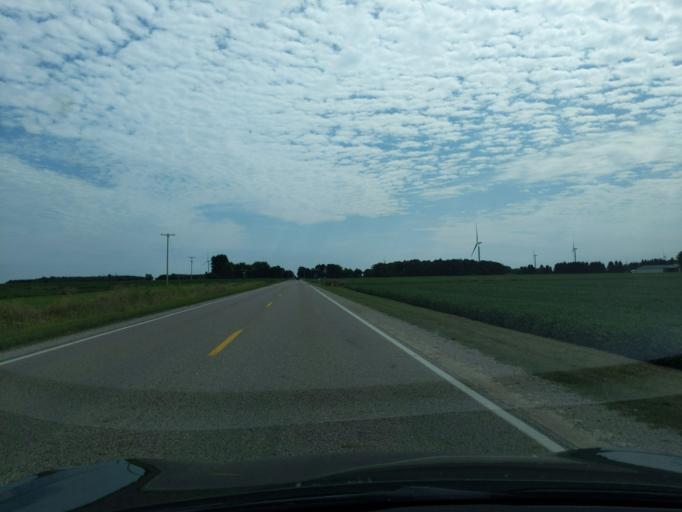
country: US
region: Michigan
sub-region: Gratiot County
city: Ithaca
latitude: 43.2916
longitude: -84.5299
